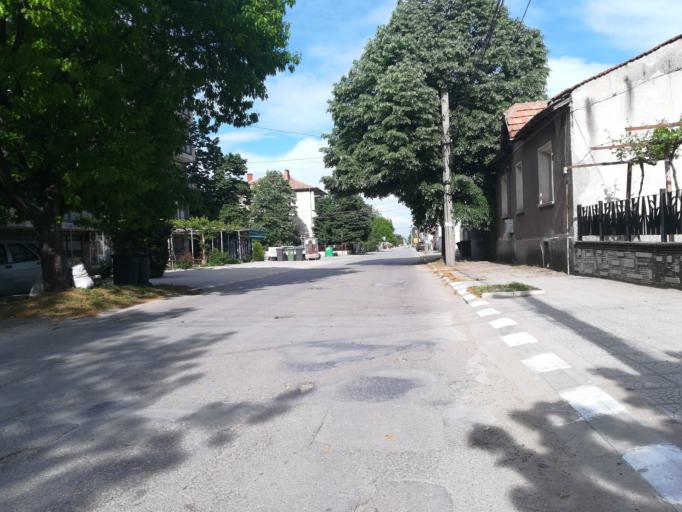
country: BG
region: Stara Zagora
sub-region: Obshtina Chirpan
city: Chirpan
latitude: 42.0964
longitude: 25.2249
